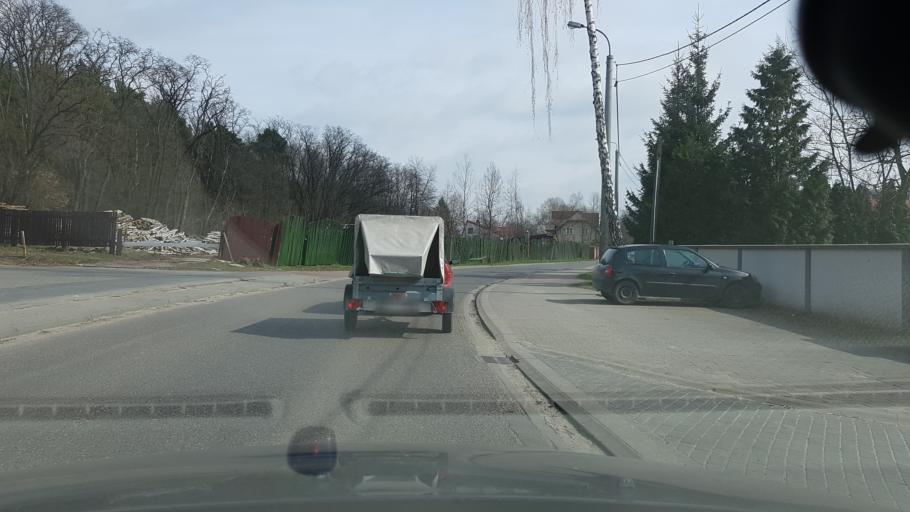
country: PL
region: Masovian Voivodeship
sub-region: Warszawa
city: Wesola
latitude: 52.2252
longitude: 21.2253
